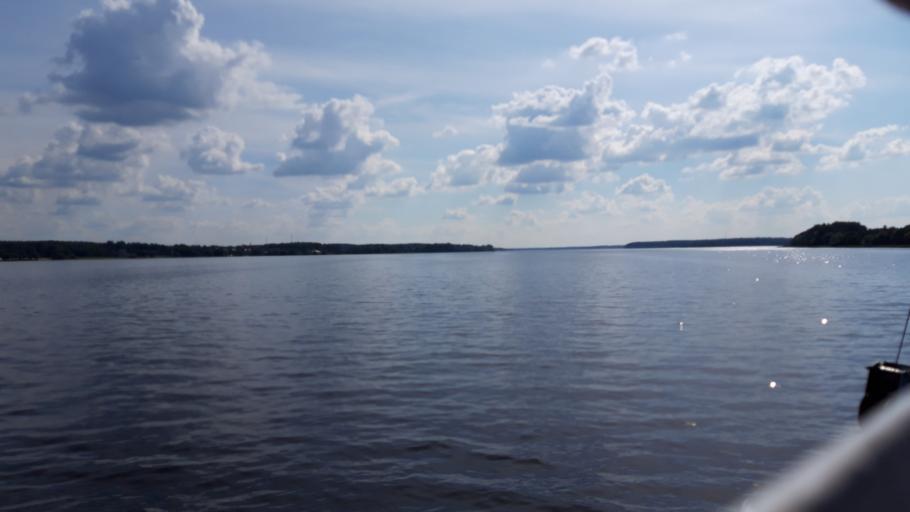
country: RU
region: Tverskaya
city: Konakovo
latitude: 56.6788
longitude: 36.6781
